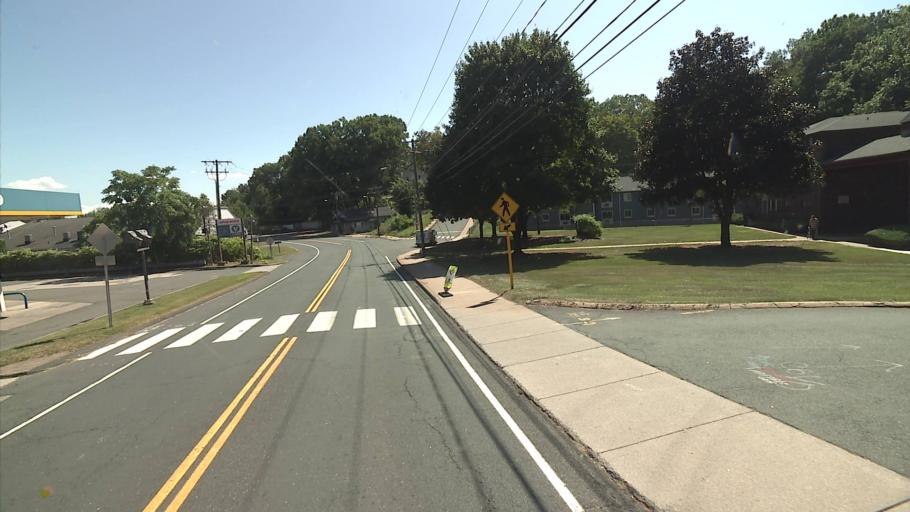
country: US
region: Connecticut
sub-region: Hartford County
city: Windsor Locks
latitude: 41.9348
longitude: -72.6299
